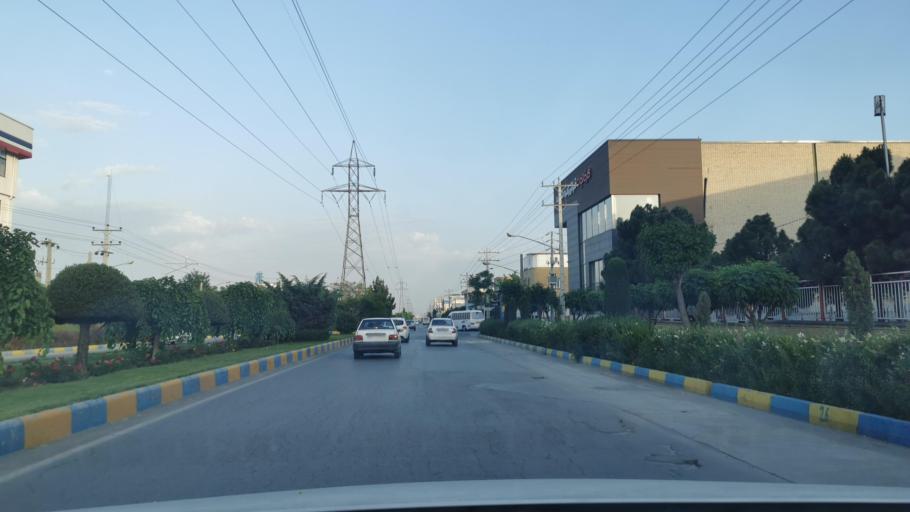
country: IR
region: Razavi Khorasan
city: Torqabeh
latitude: 36.4270
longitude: 59.4215
